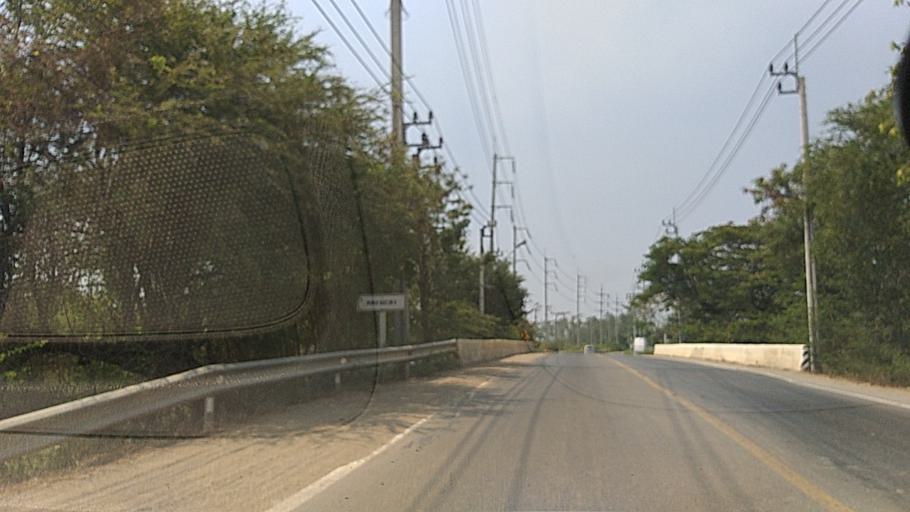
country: TH
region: Nonthaburi
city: Sai Noi
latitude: 13.9320
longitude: 100.3177
